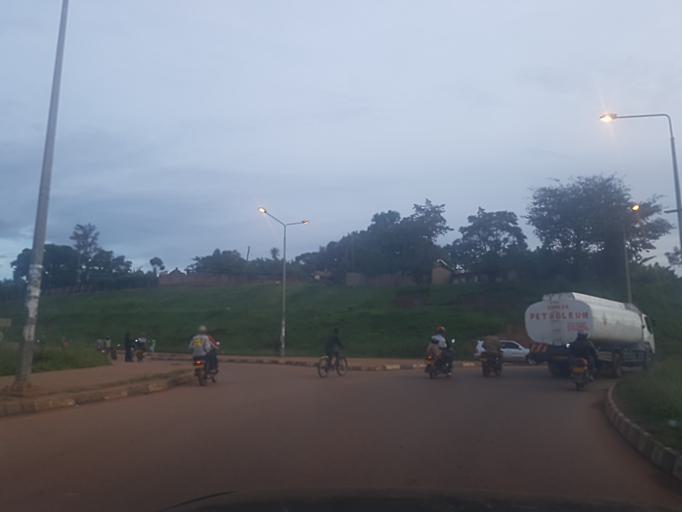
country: UG
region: Central Region
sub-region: Wakiso District
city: Kireka
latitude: 0.3653
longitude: 32.6052
